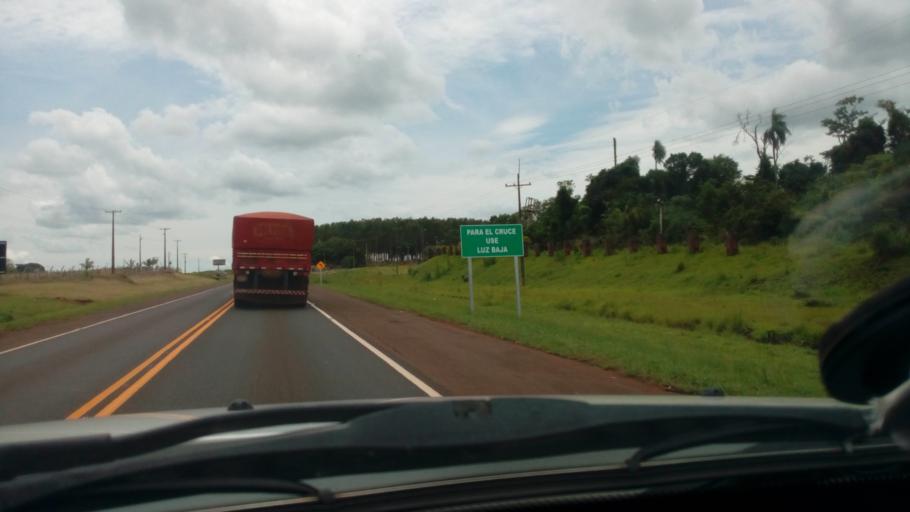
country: PY
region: Alto Parana
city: Colonia Yguazu
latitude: -25.6068
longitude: -54.9385
